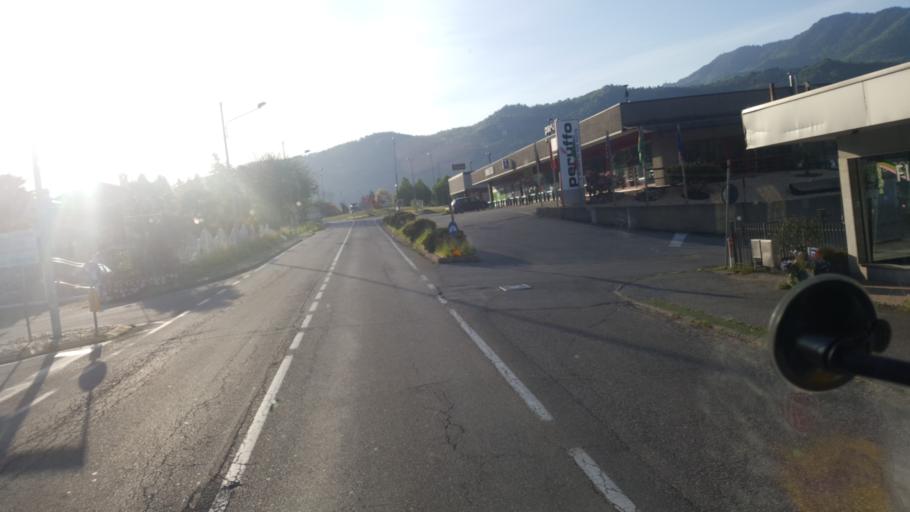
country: IT
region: Lombardy
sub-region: Provincia di Varese
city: Cuveglio
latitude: 45.9058
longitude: 8.7246
